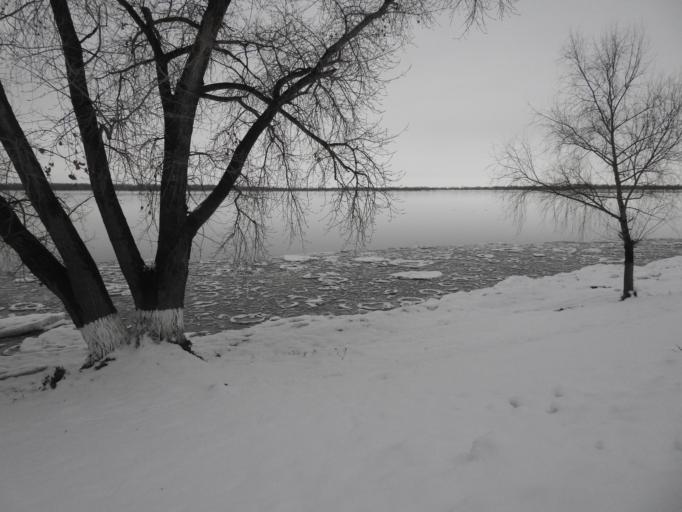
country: RU
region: Saratov
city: Vol'sk
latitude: 52.0389
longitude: 47.3964
